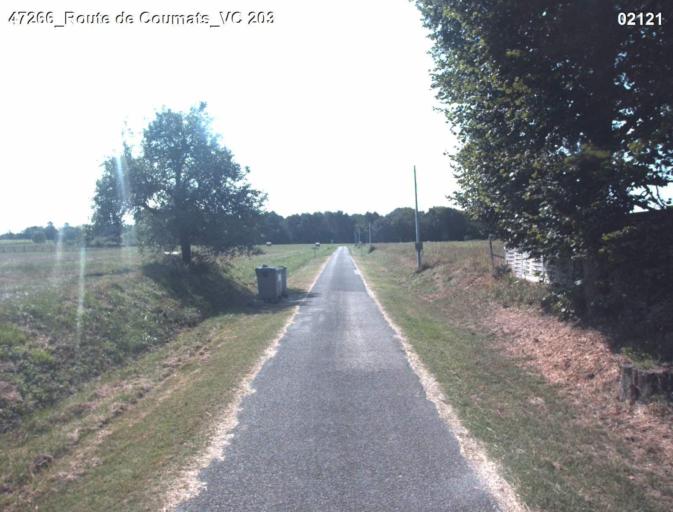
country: FR
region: Aquitaine
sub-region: Departement des Landes
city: Gabarret
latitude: 44.0038
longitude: 0.1013
